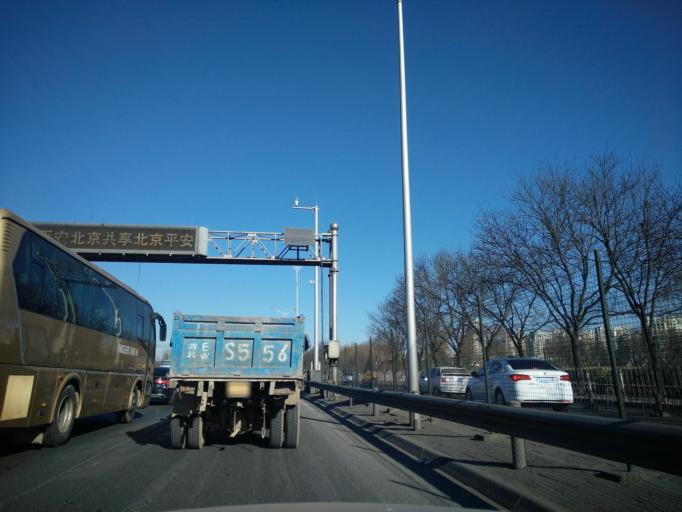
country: CN
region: Beijing
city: Huaxiang
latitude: 39.8374
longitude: 116.3399
